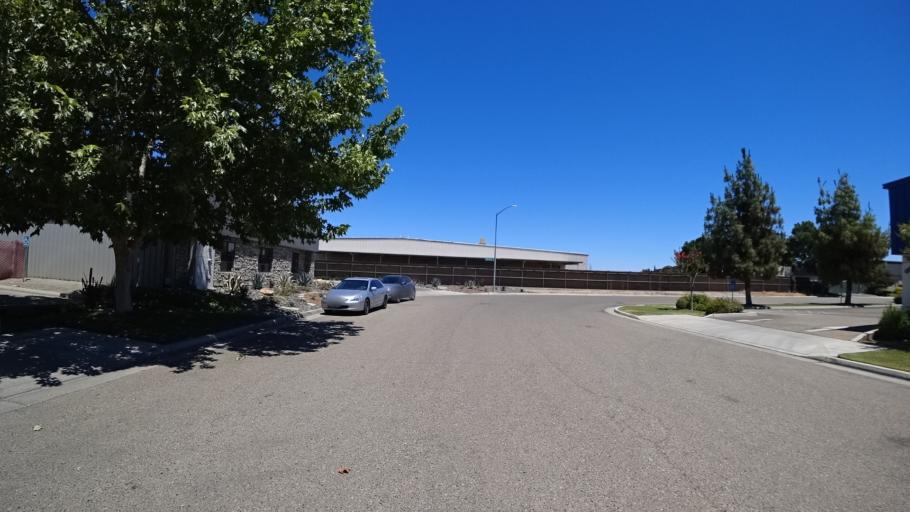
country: US
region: California
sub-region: Fresno County
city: West Park
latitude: 36.8006
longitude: -119.8585
